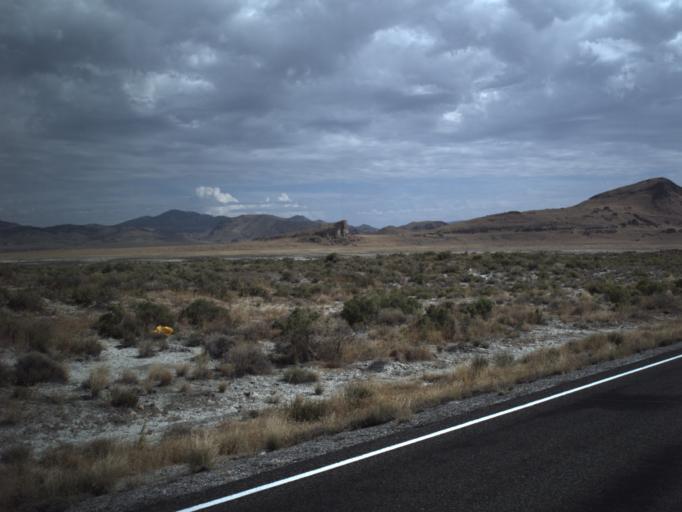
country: US
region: Utah
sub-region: Tooele County
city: Wendover
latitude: 41.4239
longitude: -113.8664
